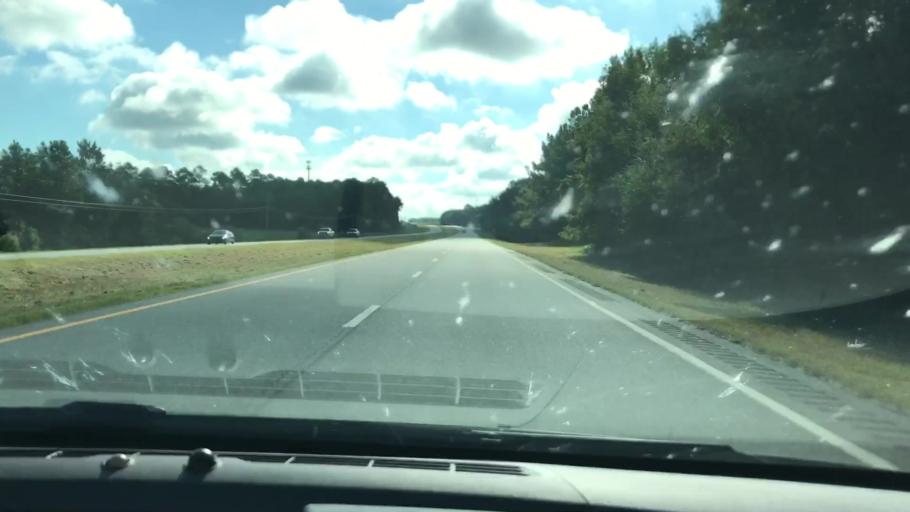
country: US
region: Georgia
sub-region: Worth County
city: Sylvester
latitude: 31.5521
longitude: -83.9465
